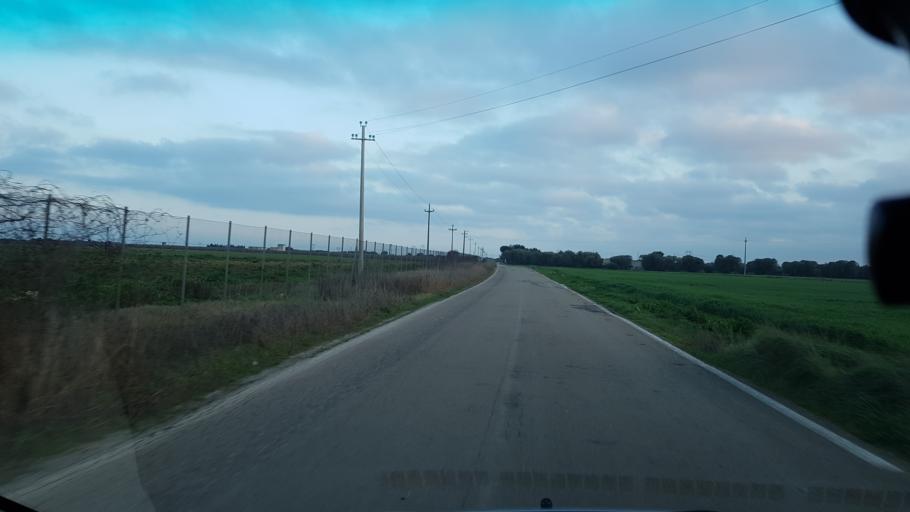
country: IT
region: Apulia
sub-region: Provincia di Brindisi
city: Mesagne
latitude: 40.5980
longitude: 17.7937
